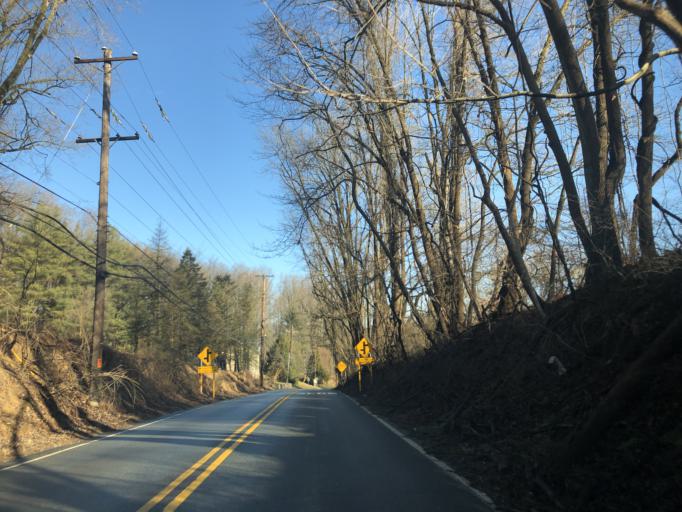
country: US
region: Pennsylvania
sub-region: Delaware County
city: Chester Heights
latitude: 39.9116
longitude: -75.4842
